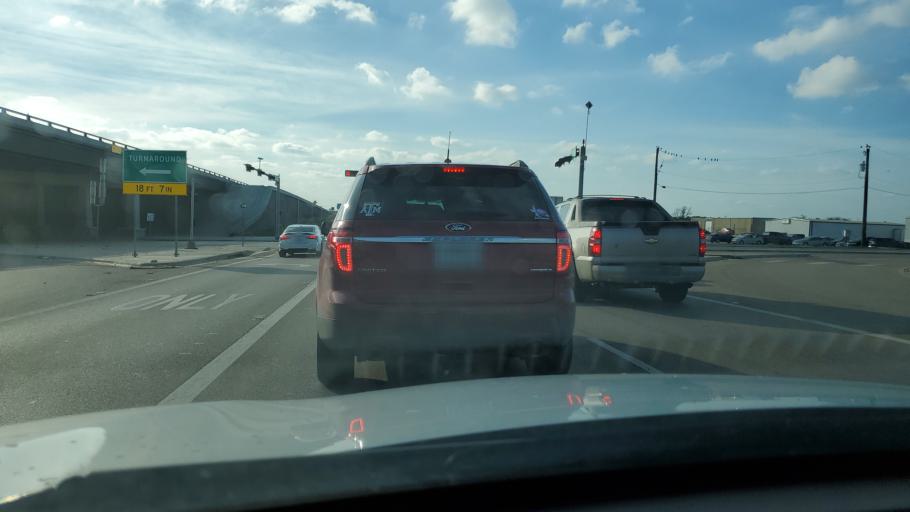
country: US
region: Texas
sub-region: Bell County
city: Harker Heights
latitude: 31.0762
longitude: -97.6874
